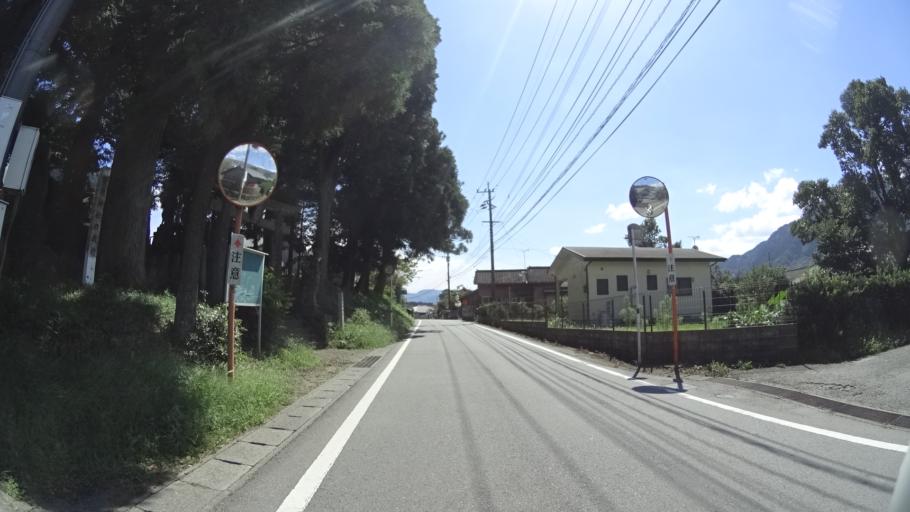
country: JP
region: Kumamoto
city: Aso
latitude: 32.9061
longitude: 130.9943
